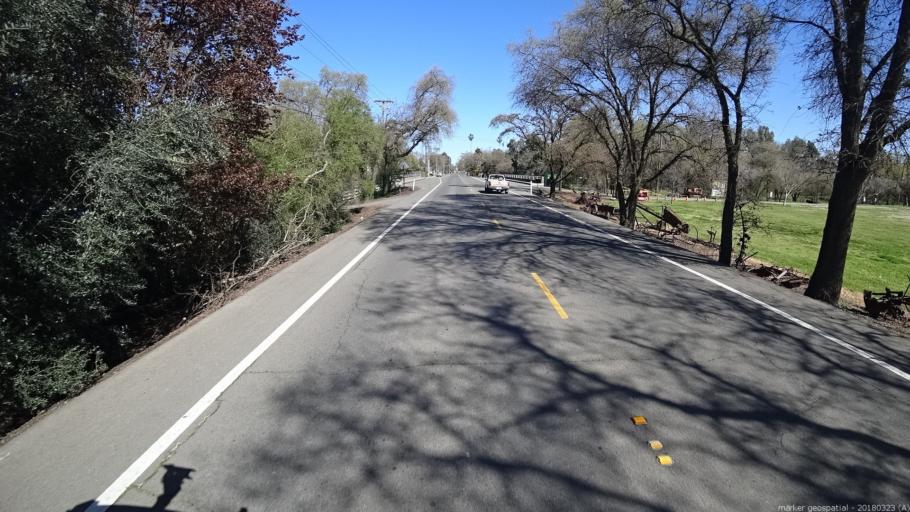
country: US
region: California
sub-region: Sacramento County
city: Rio Linda
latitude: 38.6920
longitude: -121.4384
